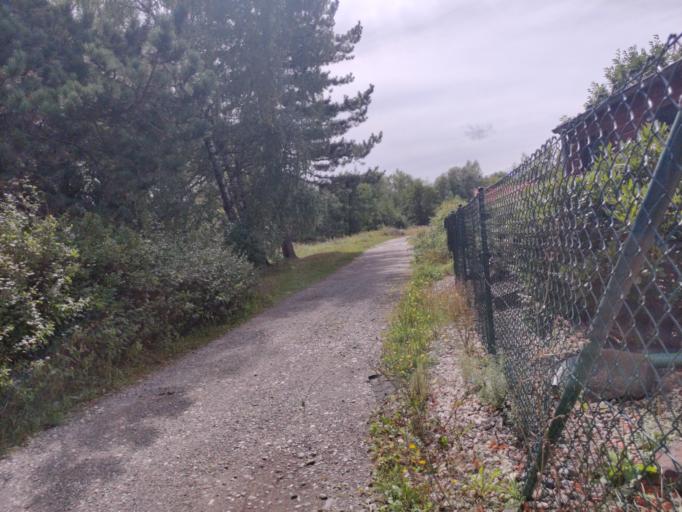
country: DE
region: Lower Saxony
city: Langelsheim
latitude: 51.9426
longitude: 10.3480
